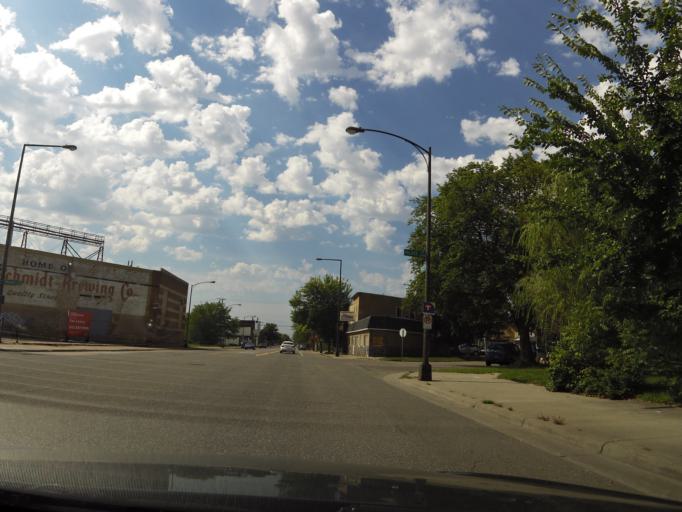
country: US
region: Minnesota
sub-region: Dakota County
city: West Saint Paul
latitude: 44.9293
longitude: -93.1245
